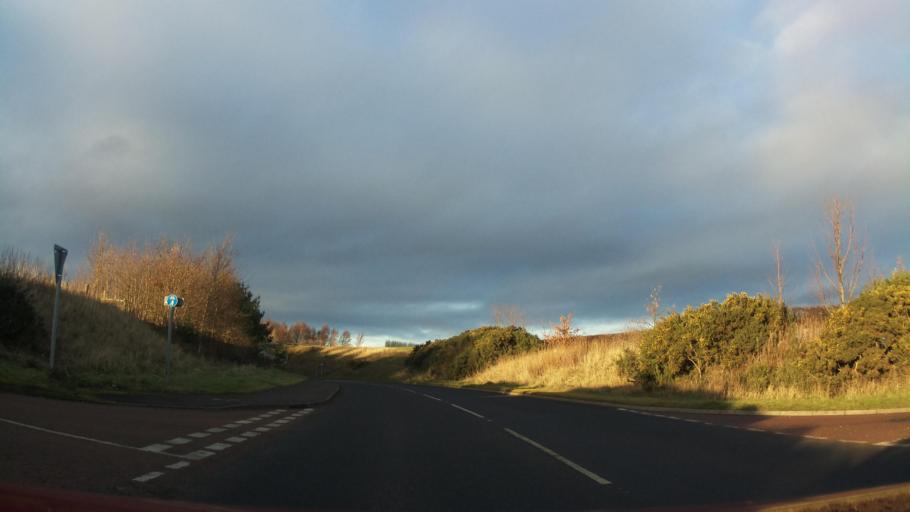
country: GB
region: Scotland
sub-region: Fife
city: Tayport
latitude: 56.4975
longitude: -2.8035
